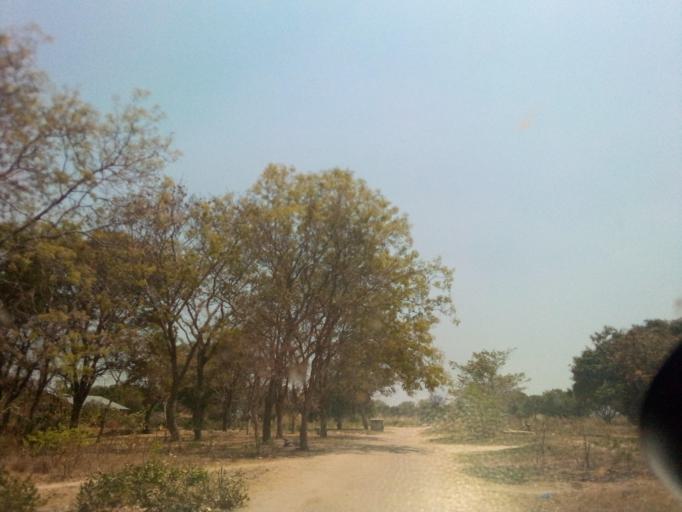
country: ZM
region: Copperbelt
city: Kataba
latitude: -12.2377
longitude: 30.3129
